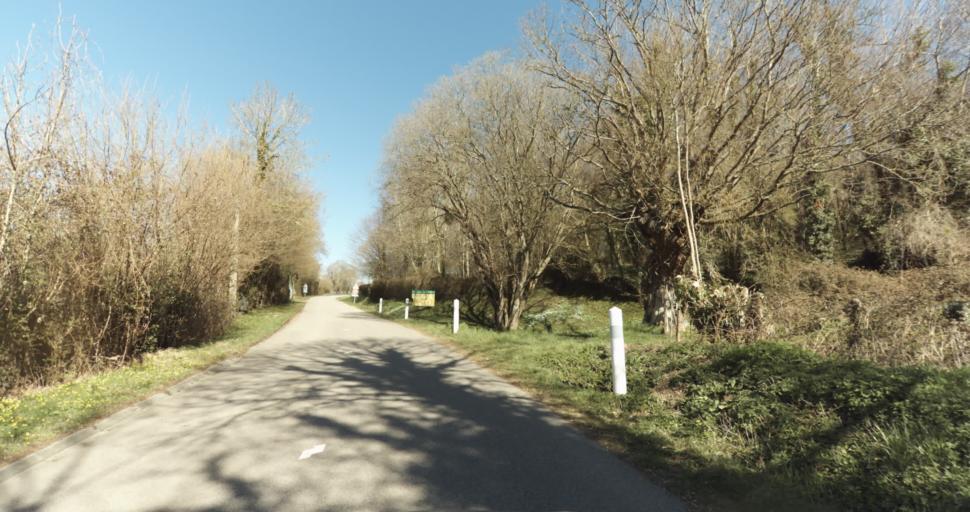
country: FR
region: Lower Normandy
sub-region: Departement du Calvados
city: Livarot
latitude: 48.9678
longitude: 0.0688
